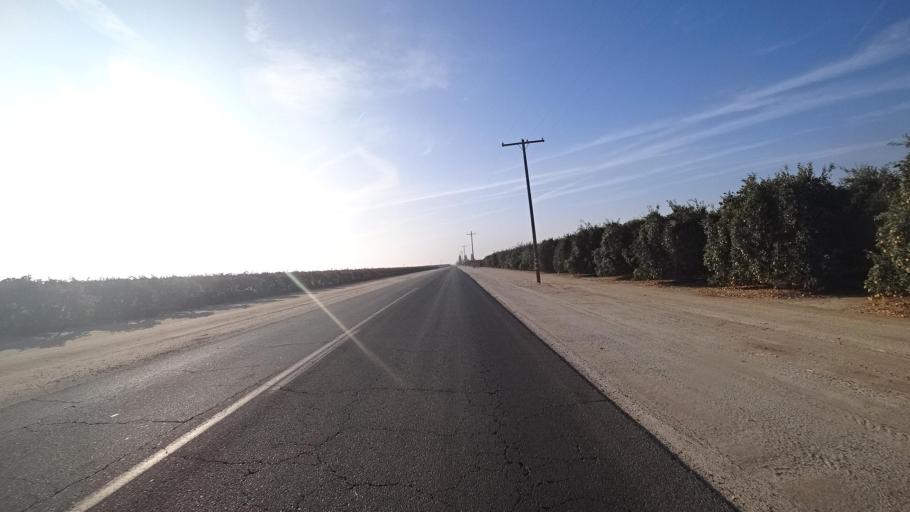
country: US
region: California
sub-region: Kern County
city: Delano
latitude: 35.7681
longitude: -119.1875
